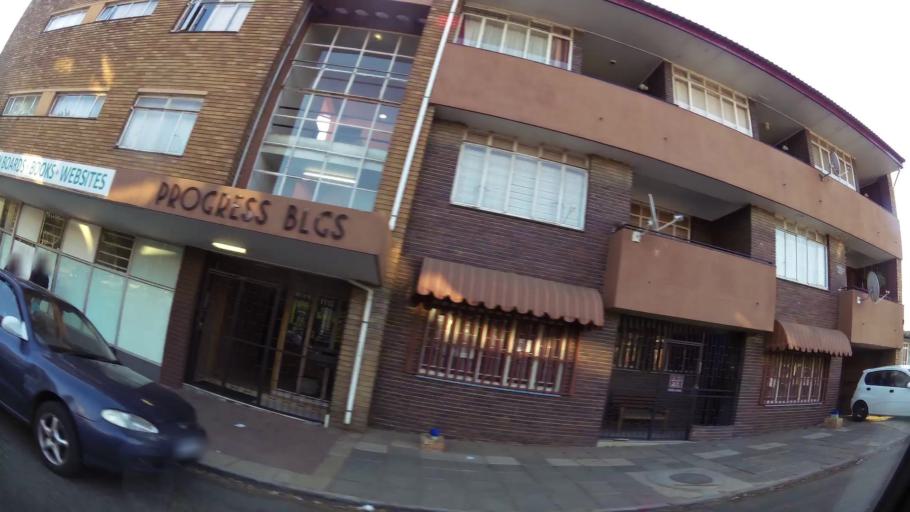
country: ZA
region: Gauteng
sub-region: Ekurhuleni Metropolitan Municipality
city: Germiston
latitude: -26.2570
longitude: 28.1301
